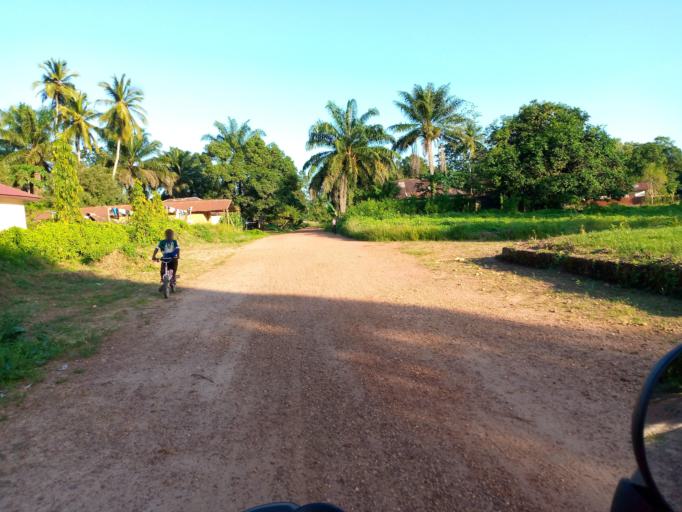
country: SL
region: Northern Province
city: Yonibana
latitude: 8.4451
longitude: -12.2401
